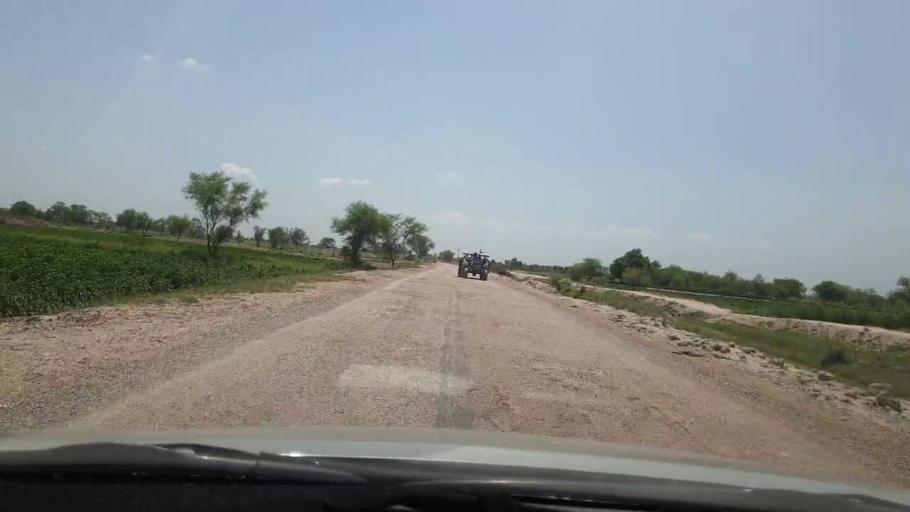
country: PK
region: Sindh
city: Pano Aqil
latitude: 27.7218
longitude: 69.1754
